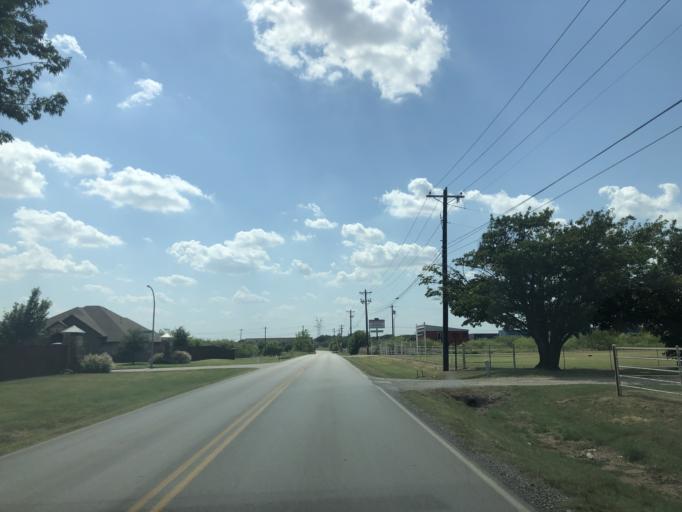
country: US
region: Texas
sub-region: Tarrant County
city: Haslet
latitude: 32.9313
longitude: -97.3278
